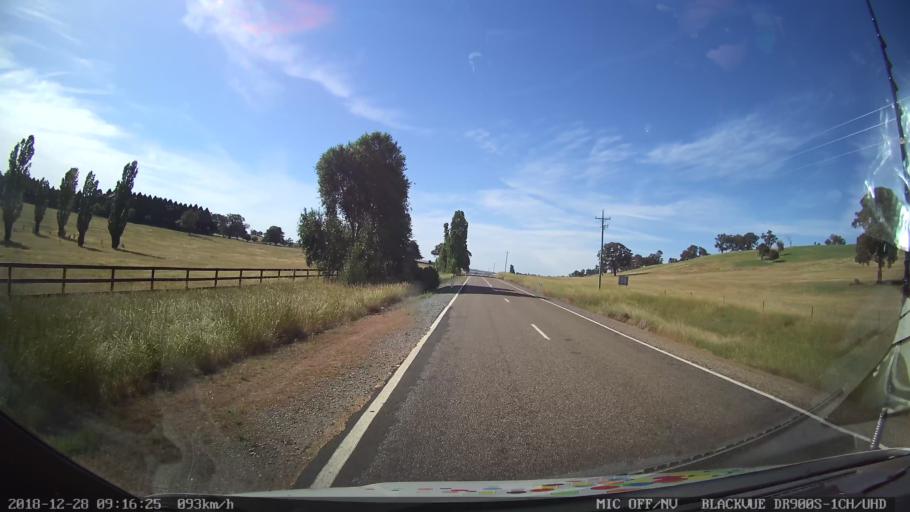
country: AU
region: New South Wales
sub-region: Upper Lachlan Shire
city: Crookwell
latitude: -34.3082
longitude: 149.3555
